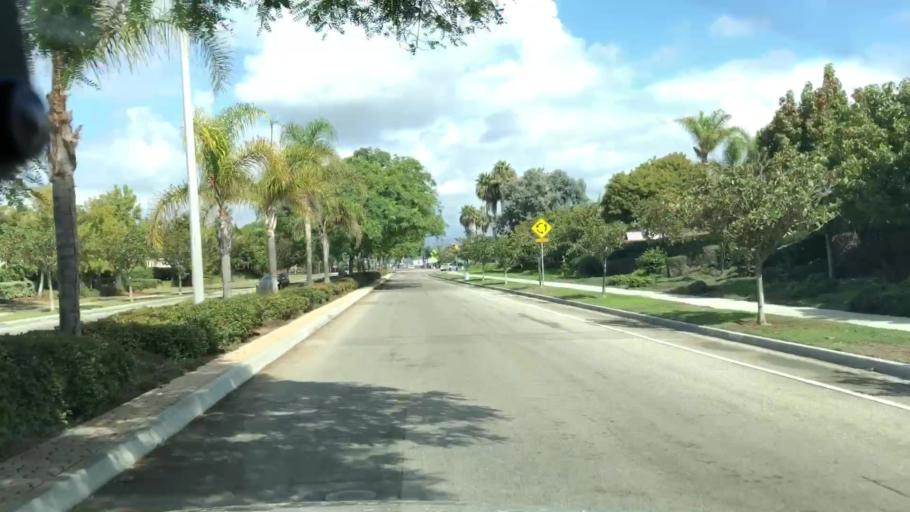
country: US
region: California
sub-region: Ventura County
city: Oxnard
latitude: 34.1947
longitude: -119.2079
